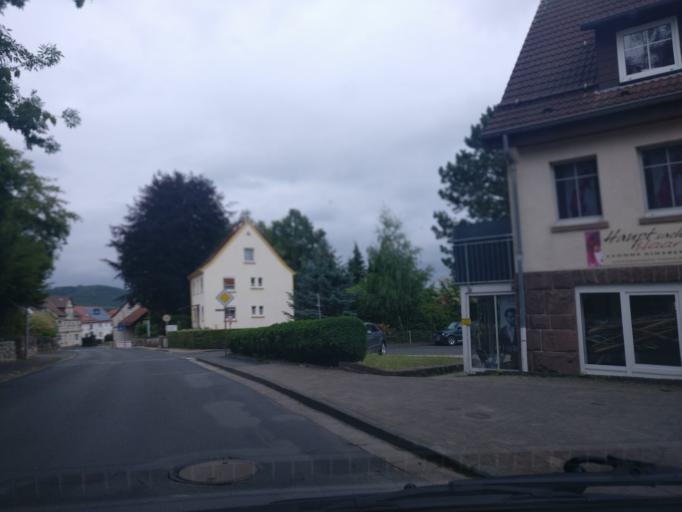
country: DE
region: Hesse
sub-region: Regierungsbezirk Kassel
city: Baunatal
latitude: 51.2744
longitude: 9.3705
